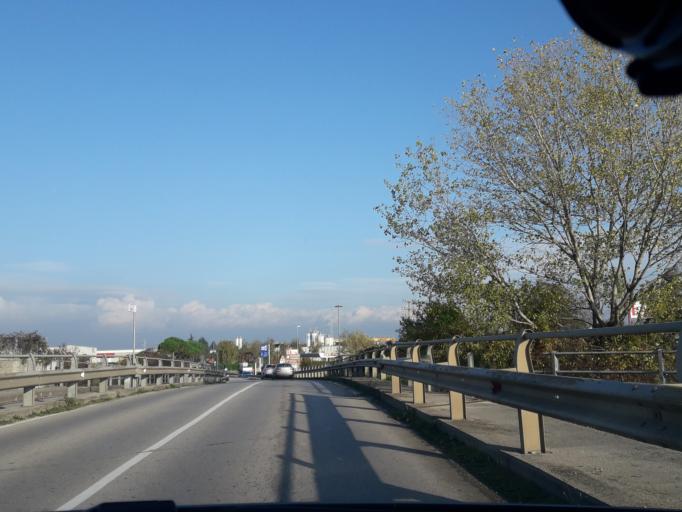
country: IT
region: Friuli Venezia Giulia
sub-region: Provincia di Udine
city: Pradamano
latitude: 46.0228
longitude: 13.2705
